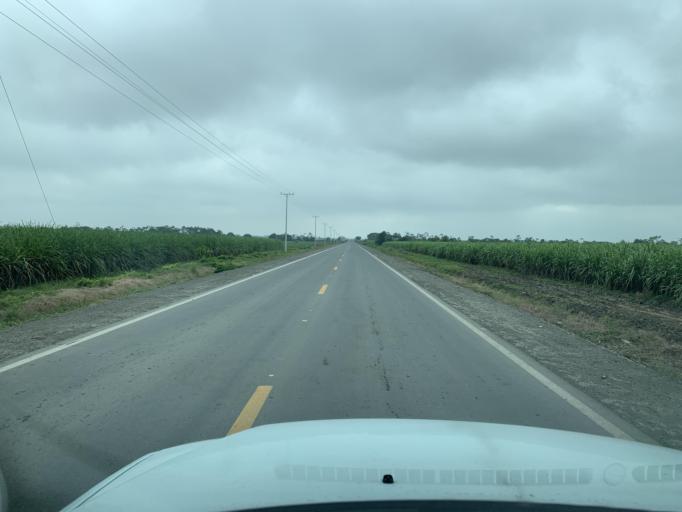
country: EC
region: Guayas
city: Coronel Marcelino Mariduena
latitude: -2.3179
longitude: -79.5164
